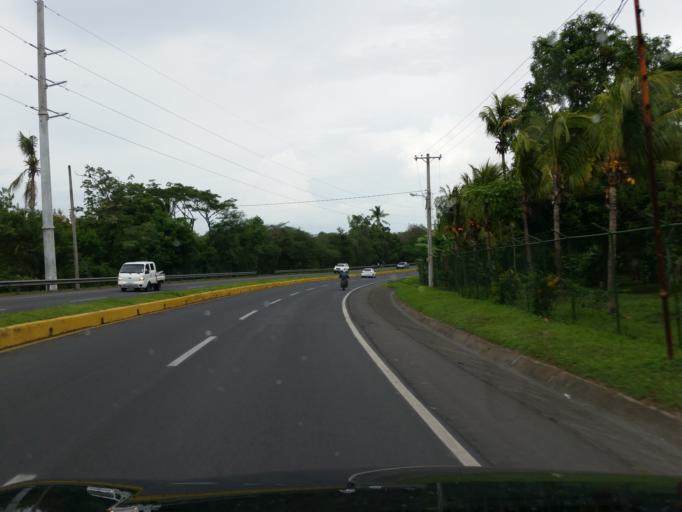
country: NI
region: Masaya
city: Masaya
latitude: 11.9787
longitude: -86.0532
